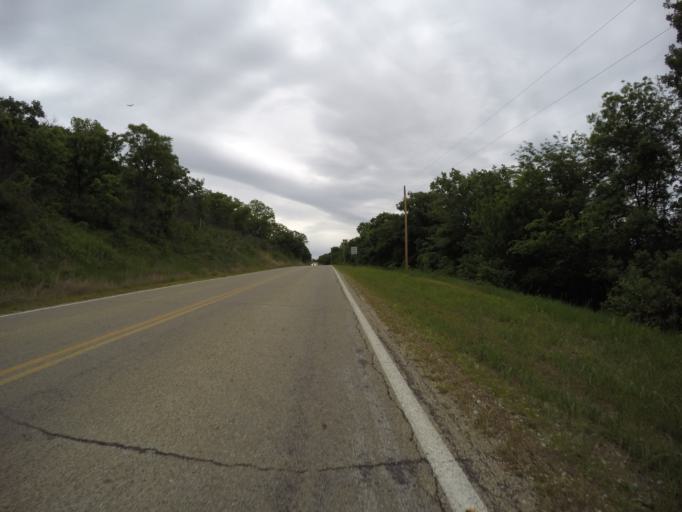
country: US
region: Kansas
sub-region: Pottawatomie County
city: Wamego
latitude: 39.1833
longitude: -96.3556
